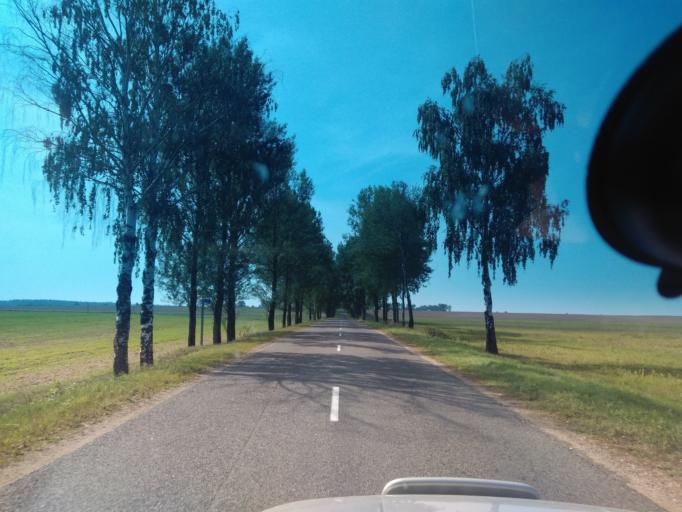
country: BY
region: Minsk
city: Kapyl'
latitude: 53.2696
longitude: 27.2017
